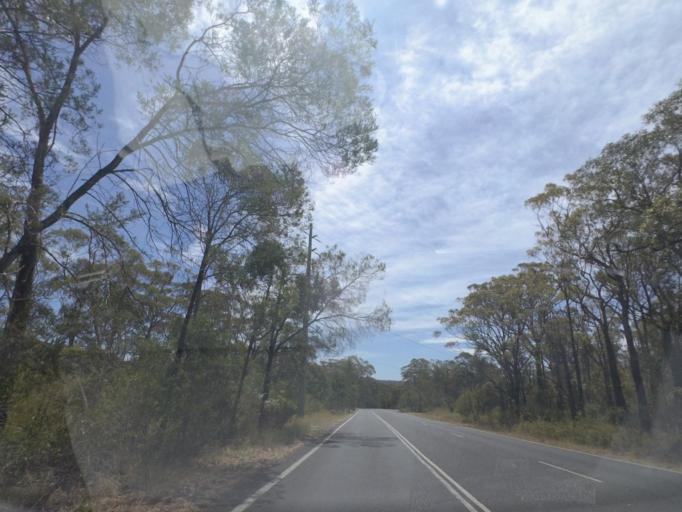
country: AU
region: New South Wales
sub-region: Wingecarribee
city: Colo Vale
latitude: -34.3940
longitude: 150.5323
